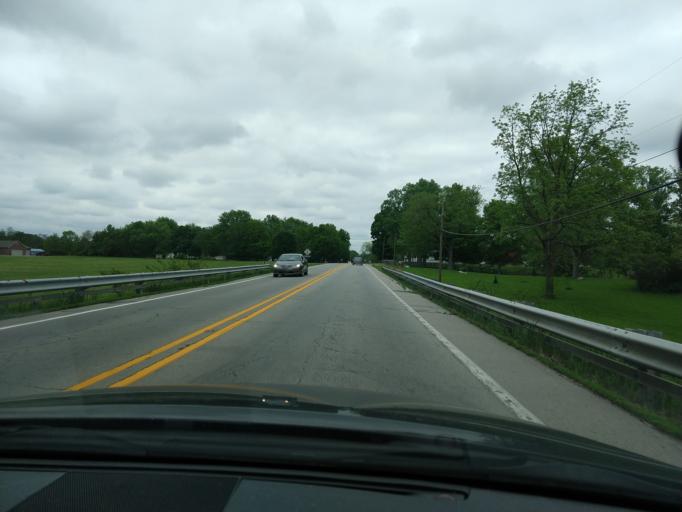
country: US
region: Indiana
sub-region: Madison County
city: Lapel
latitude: 40.0677
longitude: -85.8662
